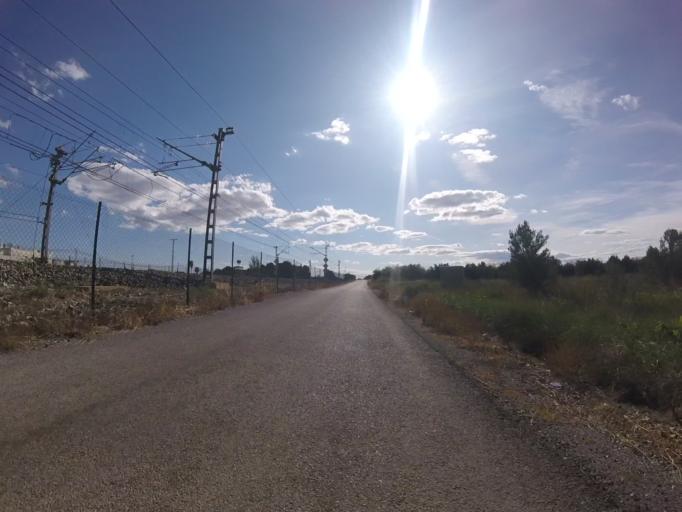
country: ES
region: Valencia
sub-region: Provincia de Castello
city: Alcala de Xivert
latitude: 40.2964
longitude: 0.2255
